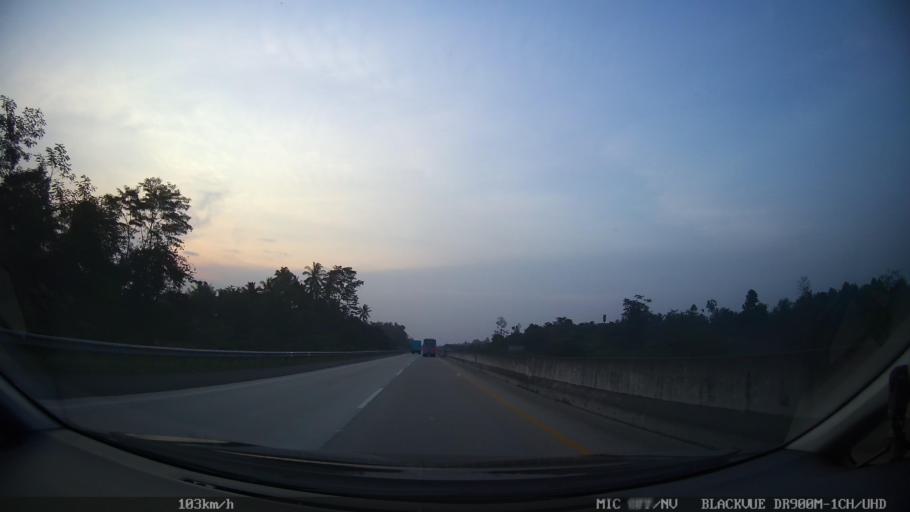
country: ID
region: Lampung
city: Pasuruan
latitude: -5.7053
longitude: 105.6394
